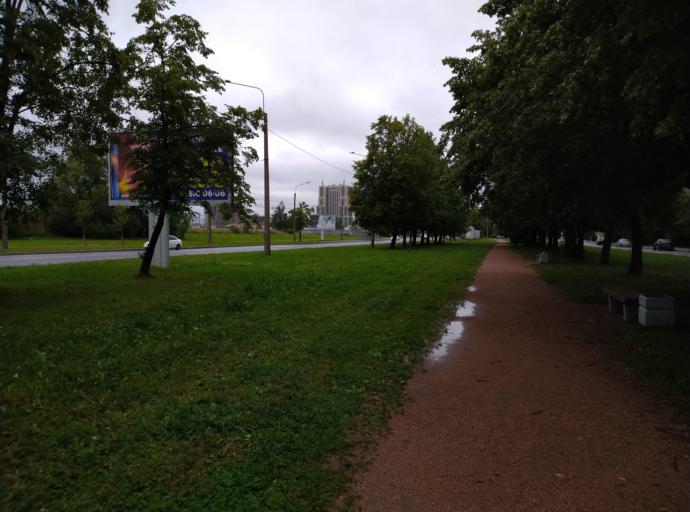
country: RU
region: St.-Petersburg
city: Kupchino
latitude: 59.8466
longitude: 30.3555
